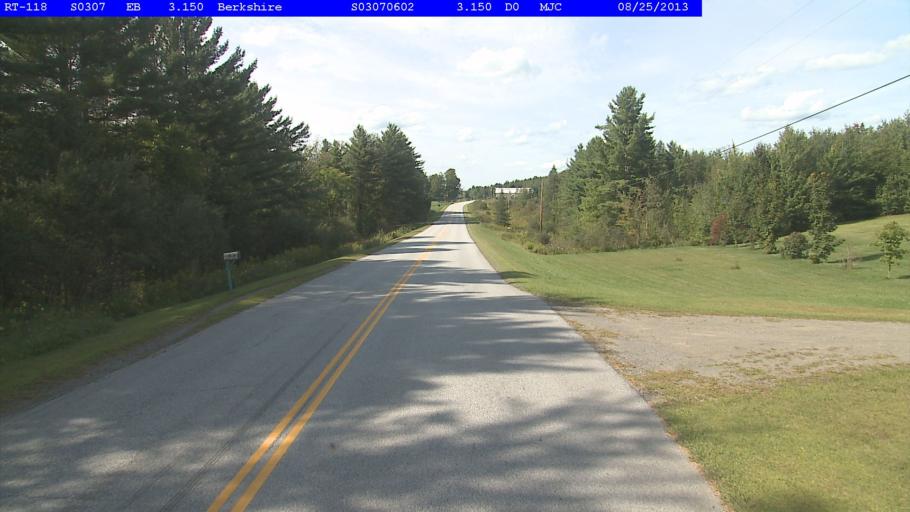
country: US
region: Vermont
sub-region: Franklin County
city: Enosburg Falls
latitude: 44.9610
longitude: -72.7576
